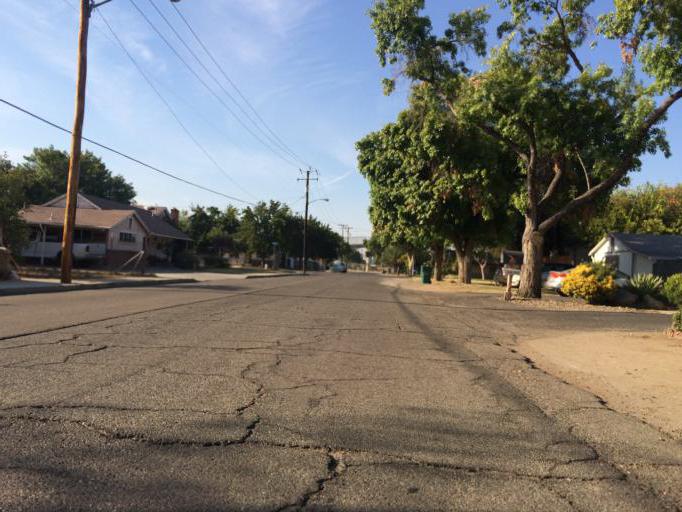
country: US
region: California
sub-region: Fresno County
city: Sunnyside
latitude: 36.7515
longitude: -119.7319
